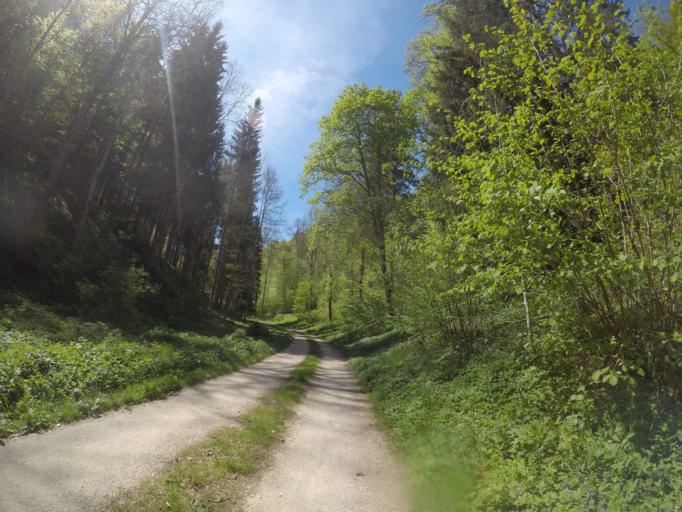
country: DE
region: Baden-Wuerttemberg
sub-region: Tuebingen Region
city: Schelklingen
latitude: 48.4261
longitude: 9.6982
